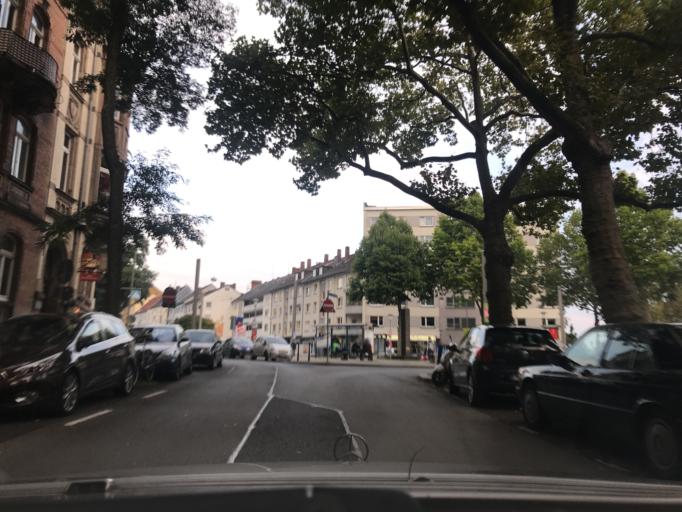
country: DE
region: Hesse
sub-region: Regierungsbezirk Kassel
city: Kassel
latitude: 51.3165
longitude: 9.4684
